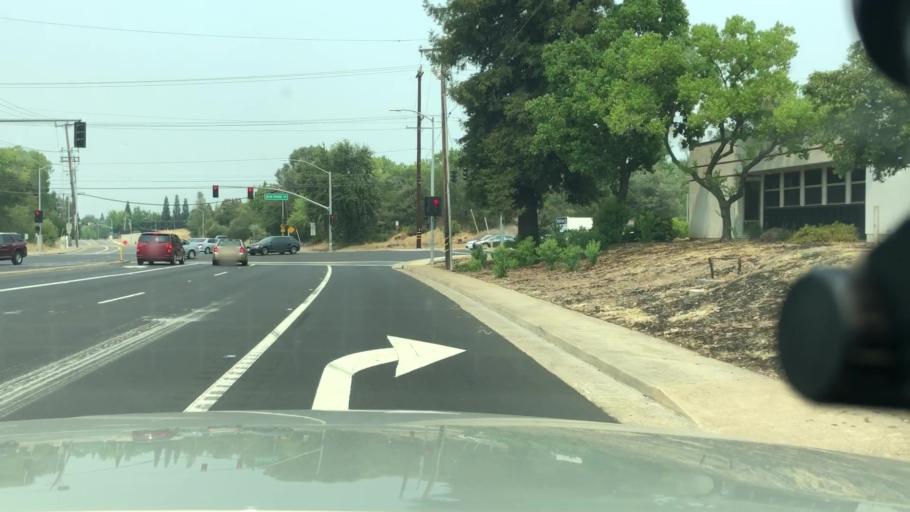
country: US
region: California
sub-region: Sacramento County
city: Folsom
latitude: 38.6558
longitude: -121.1685
